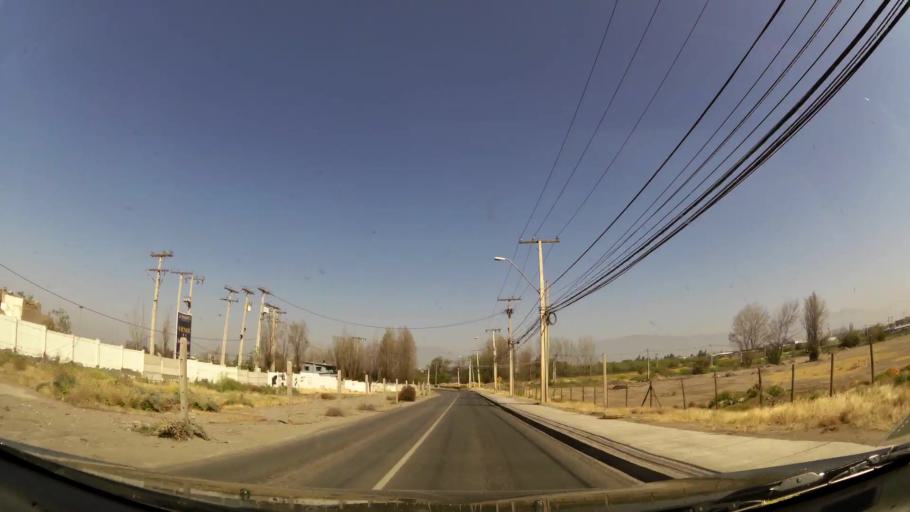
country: CL
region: Santiago Metropolitan
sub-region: Provincia de Chacabuco
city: Chicureo Abajo
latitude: -33.3168
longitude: -70.7097
